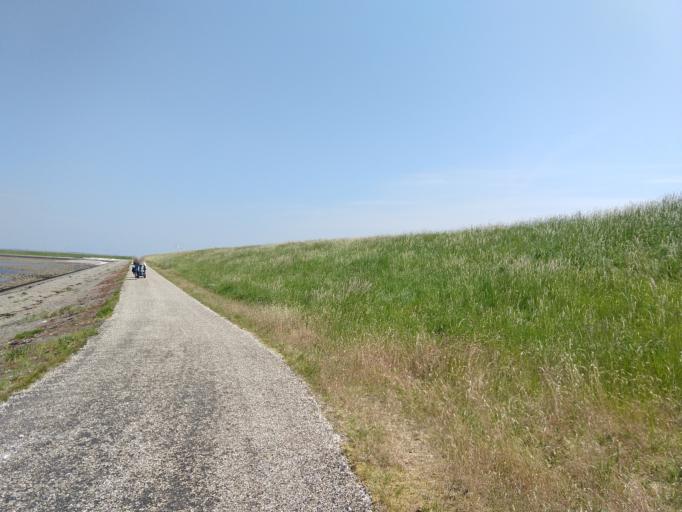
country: NL
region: Zeeland
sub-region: Schouwen-Duiveland
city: Bruinisse
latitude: 51.5948
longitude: 4.0120
